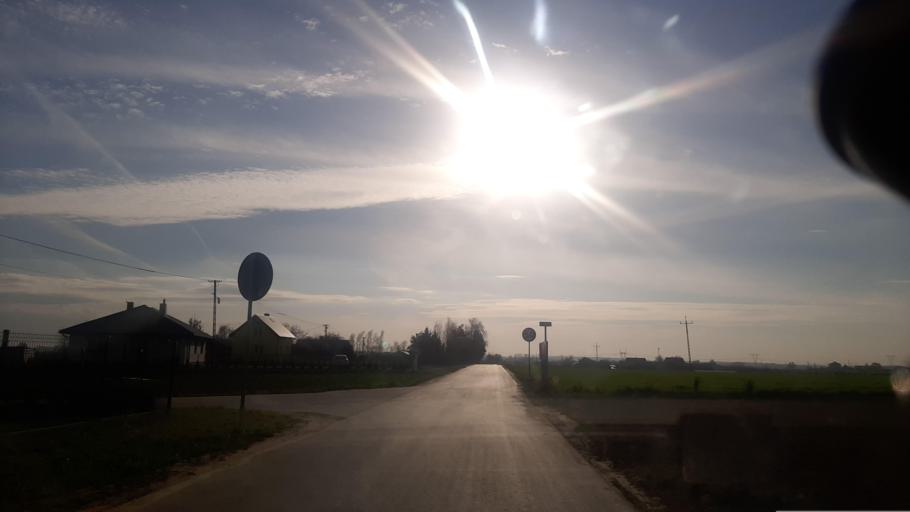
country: PL
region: Lublin Voivodeship
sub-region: Powiat lubelski
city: Garbow
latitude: 51.3846
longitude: 22.3395
